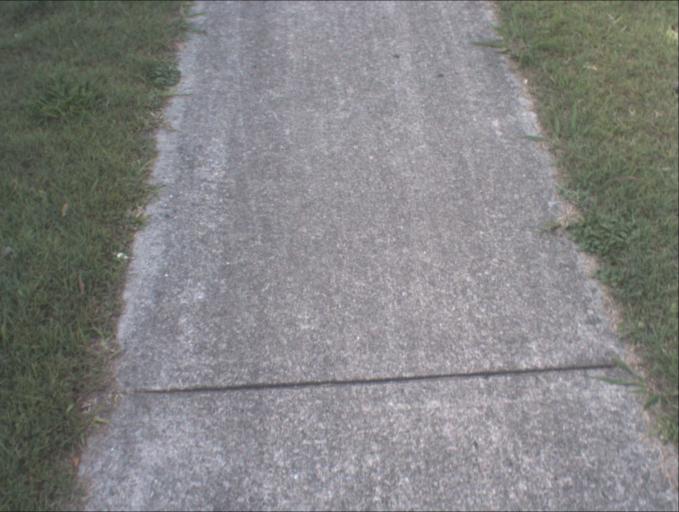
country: AU
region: Queensland
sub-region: Logan
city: Park Ridge South
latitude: -27.7091
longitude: 153.0220
